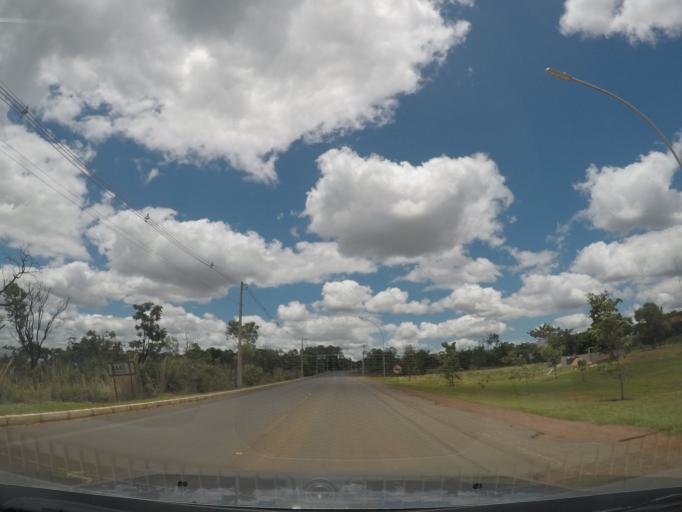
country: BR
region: Federal District
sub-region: Brasilia
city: Brasilia
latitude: -15.7758
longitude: -47.8113
